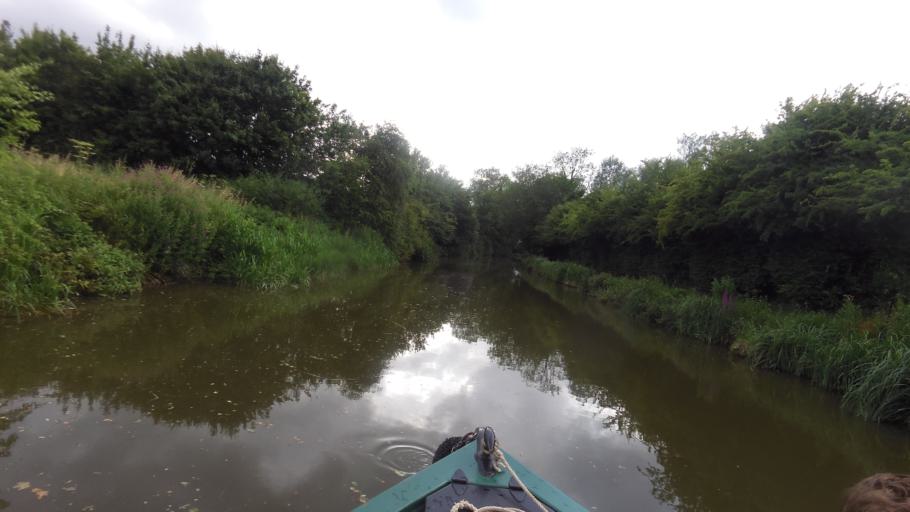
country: GB
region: England
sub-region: West Berkshire
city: Kintbury
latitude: 51.4020
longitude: -1.4329
